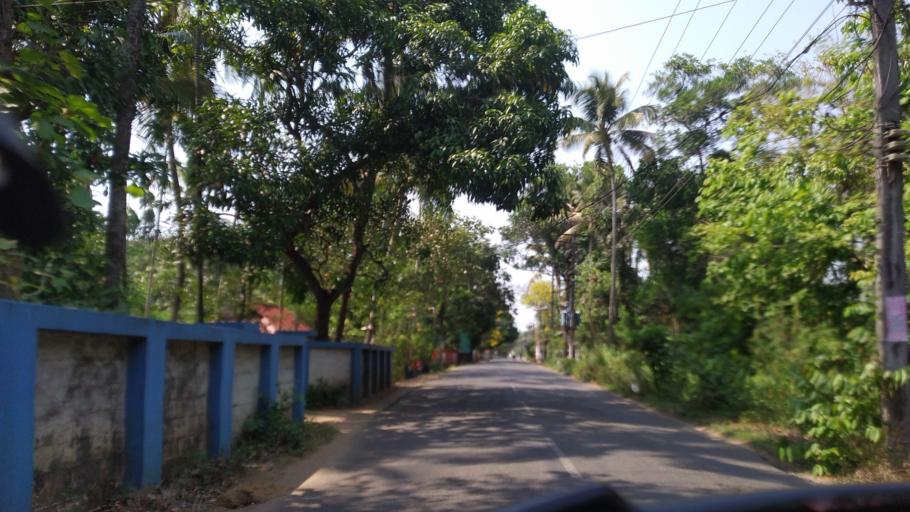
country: IN
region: Kerala
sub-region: Thrissur District
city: Kodungallur
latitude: 10.2569
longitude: 76.1460
